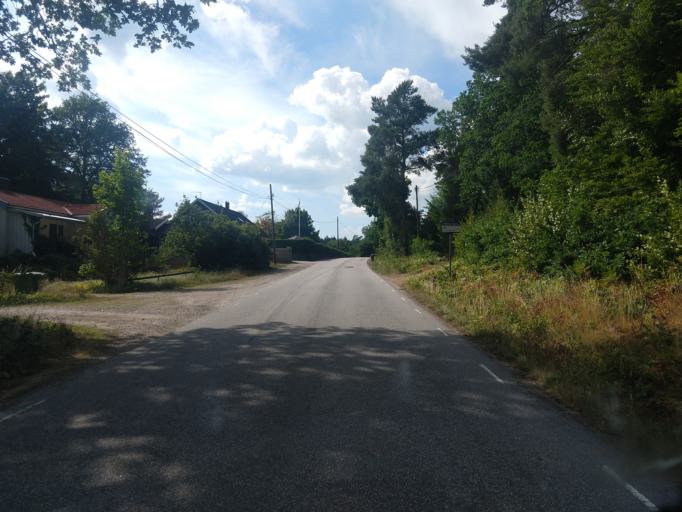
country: SE
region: Blekinge
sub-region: Karlskrona Kommun
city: Rodeby
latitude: 56.2296
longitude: 15.5819
